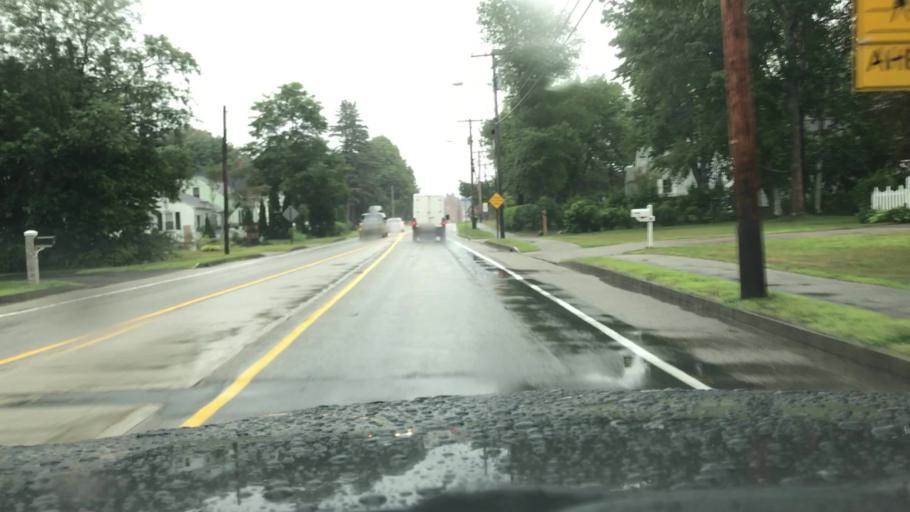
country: US
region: Maine
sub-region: York County
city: Kennebunk
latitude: 43.3990
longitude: -70.5532
